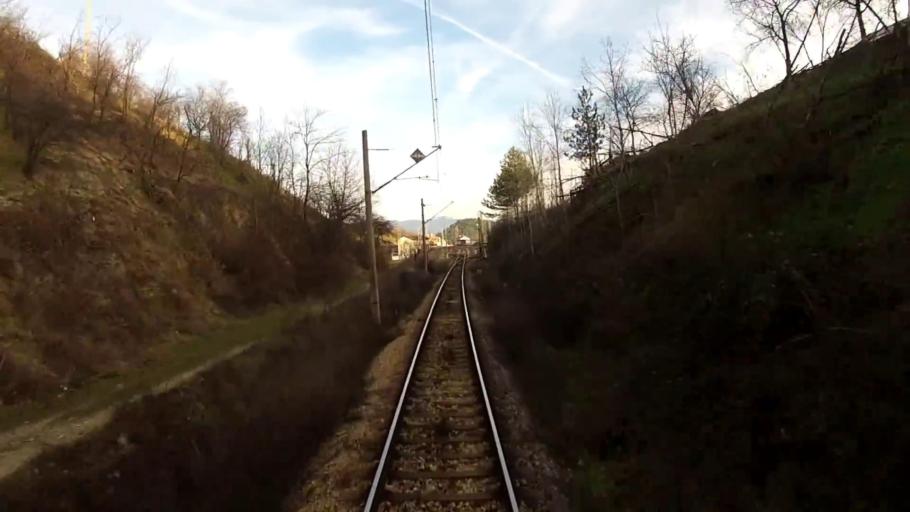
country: BG
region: Plovdiv
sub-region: Obshtina Karlovo
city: Klisura
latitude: 42.7044
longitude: 24.5026
